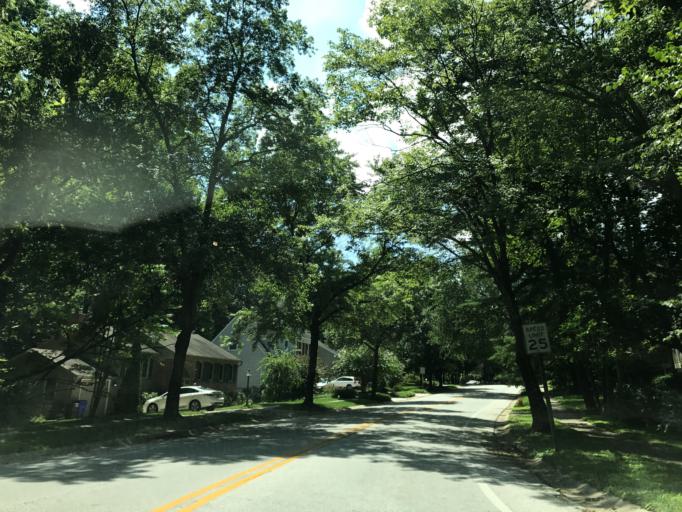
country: US
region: Maryland
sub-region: Howard County
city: Columbia
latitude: 39.2309
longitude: -76.8805
